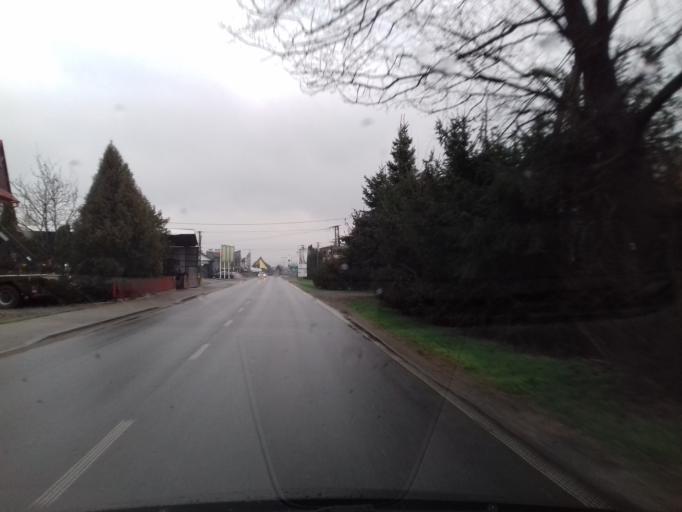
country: PL
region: Lesser Poland Voivodeship
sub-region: Powiat nowosadecki
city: Stary Sacz
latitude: 49.5993
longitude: 20.6386
